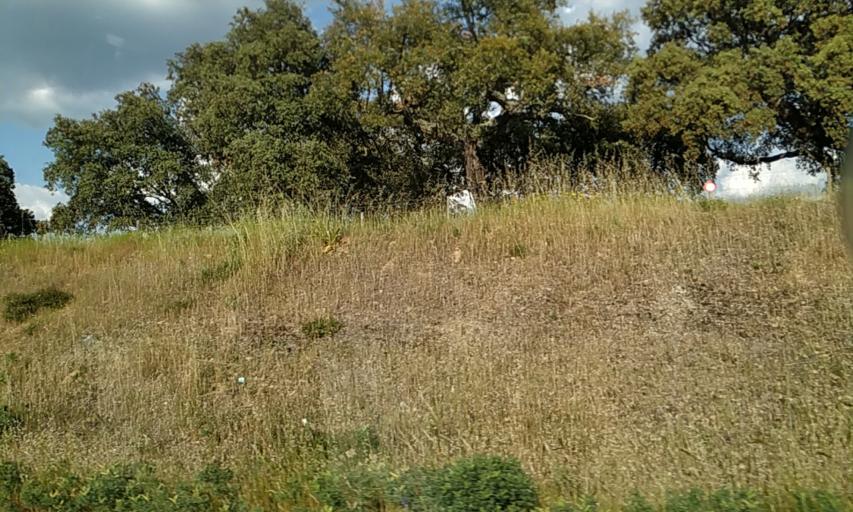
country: PT
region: Portalegre
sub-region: Portalegre
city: Urra
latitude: 39.2122
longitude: -7.4585
